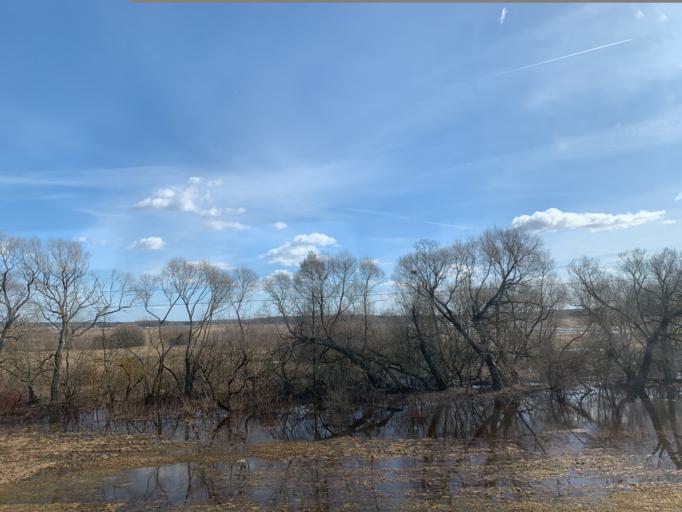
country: BY
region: Minsk
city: Stowbtsy
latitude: 53.4708
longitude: 26.7357
